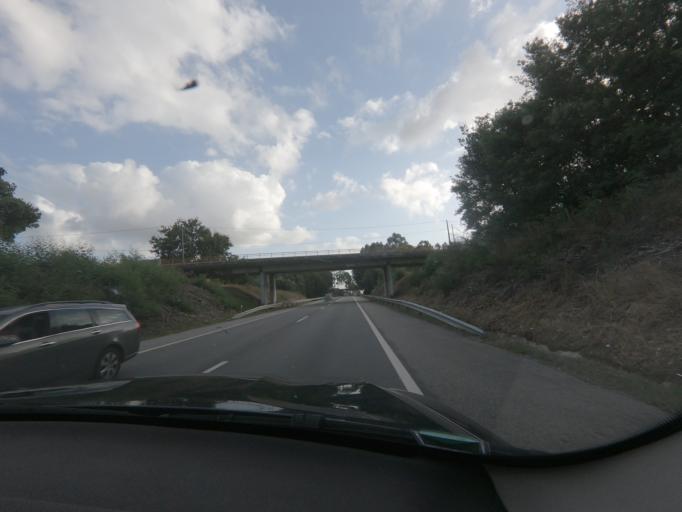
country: PT
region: Viseu
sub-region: Concelho de Tondela
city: Tondela
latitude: 40.5719
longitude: -8.0347
